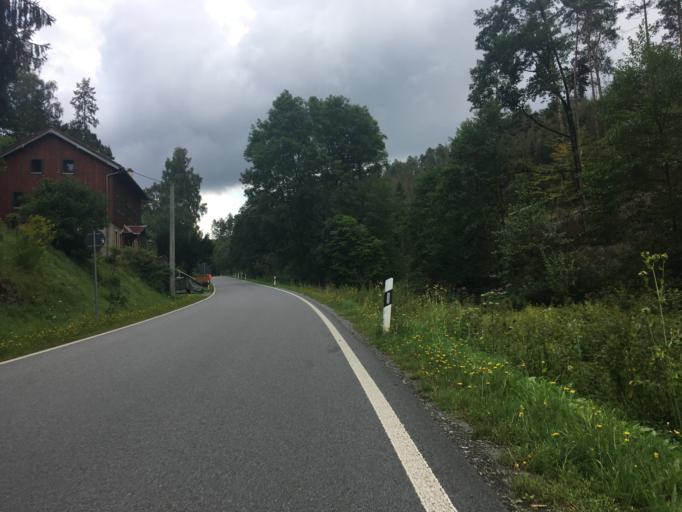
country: CZ
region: Ustecky
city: Mikulasovice
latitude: 50.9283
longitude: 14.3277
